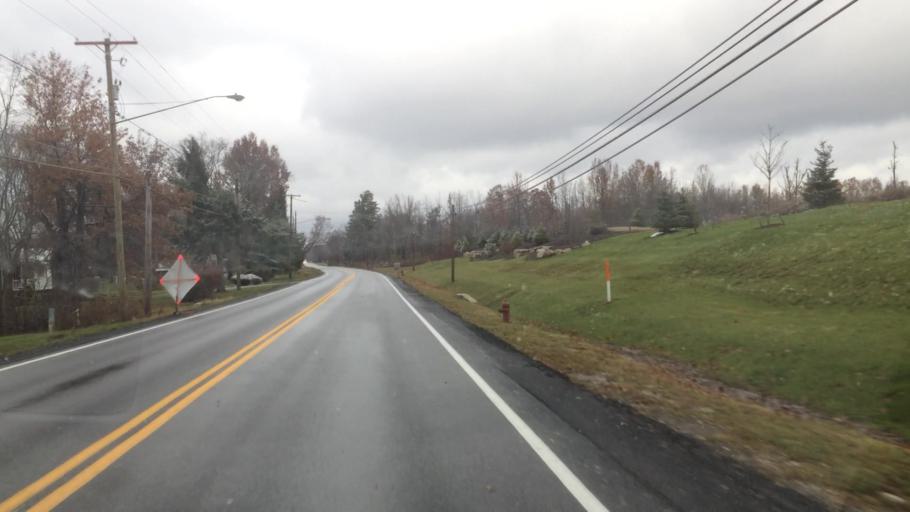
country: US
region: Ohio
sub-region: Summit County
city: Boston Heights
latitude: 41.2674
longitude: -81.5135
